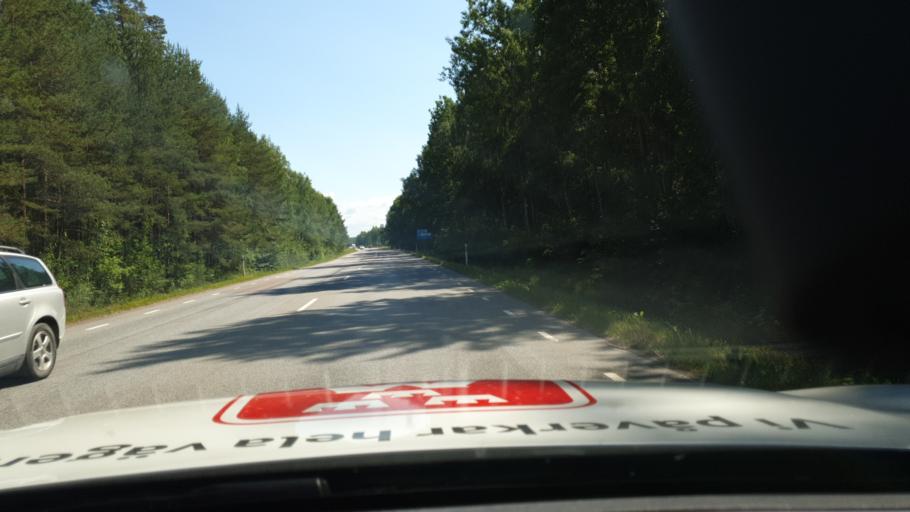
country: SE
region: Vaestra Goetaland
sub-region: Lidkopings Kommun
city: Lidkoping
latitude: 58.5143
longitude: 13.1158
